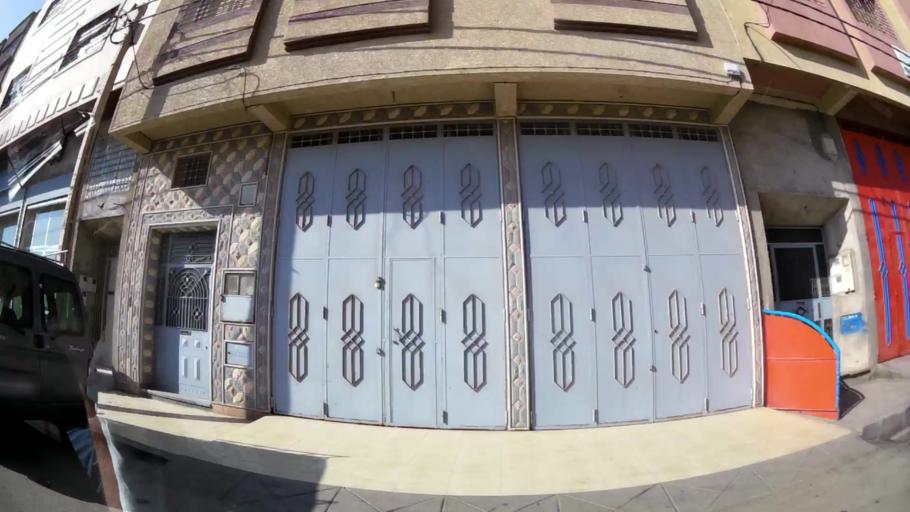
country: MA
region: Oriental
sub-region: Oujda-Angad
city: Oujda
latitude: 34.6806
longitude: -1.9429
